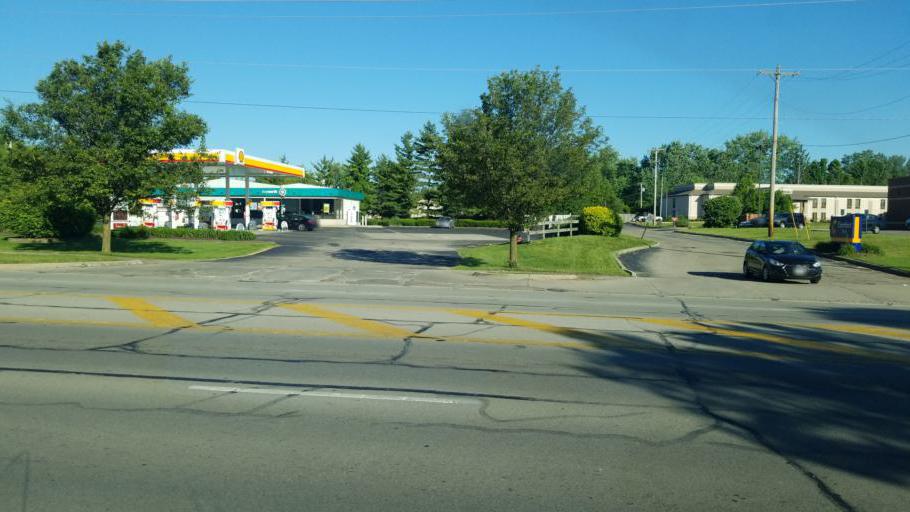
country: US
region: Ohio
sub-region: Montgomery County
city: Huber Heights
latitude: 39.8657
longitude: -84.1015
